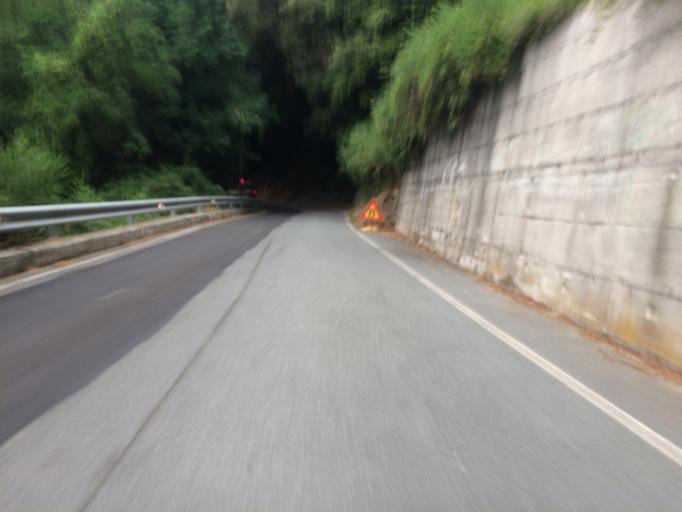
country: IT
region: Liguria
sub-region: Provincia di Imperia
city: Seborga
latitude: 43.8486
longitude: 7.7381
